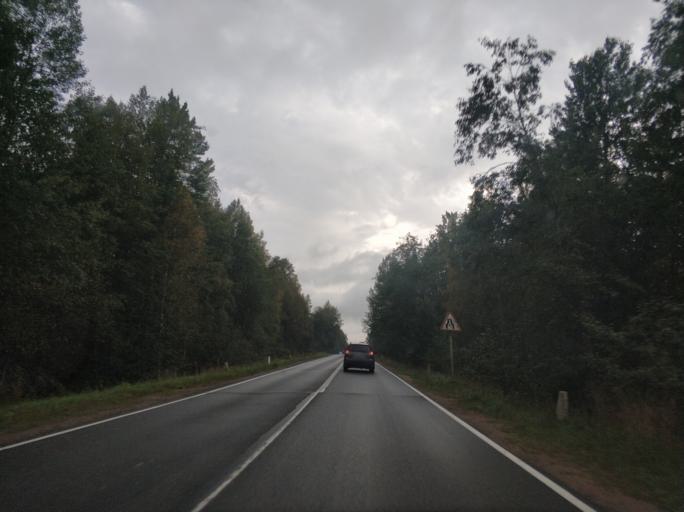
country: RU
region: Leningrad
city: Borisova Griva
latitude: 60.1338
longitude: 30.9615
